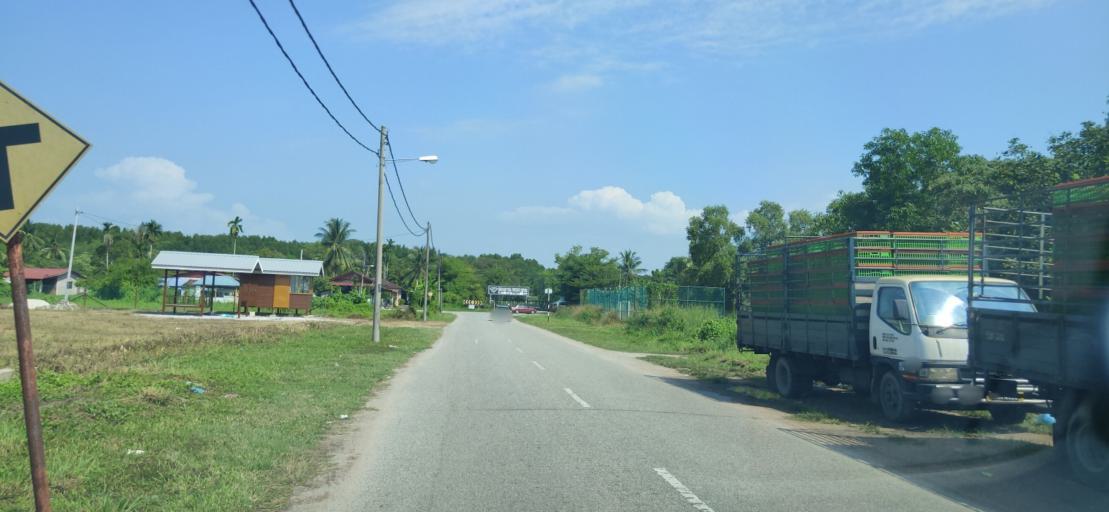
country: MY
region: Kedah
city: Sungai Petani
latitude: 5.6618
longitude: 100.4612
